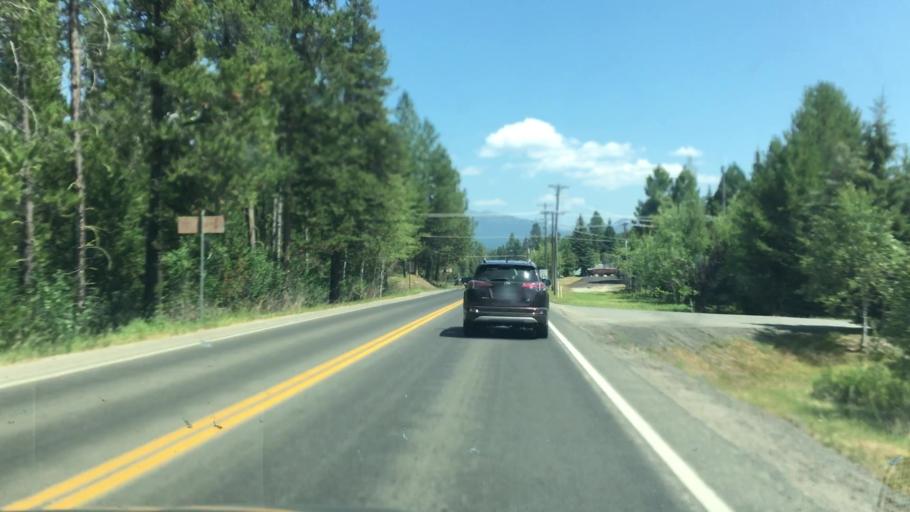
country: US
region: Idaho
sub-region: Valley County
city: McCall
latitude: 44.9133
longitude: -116.1253
